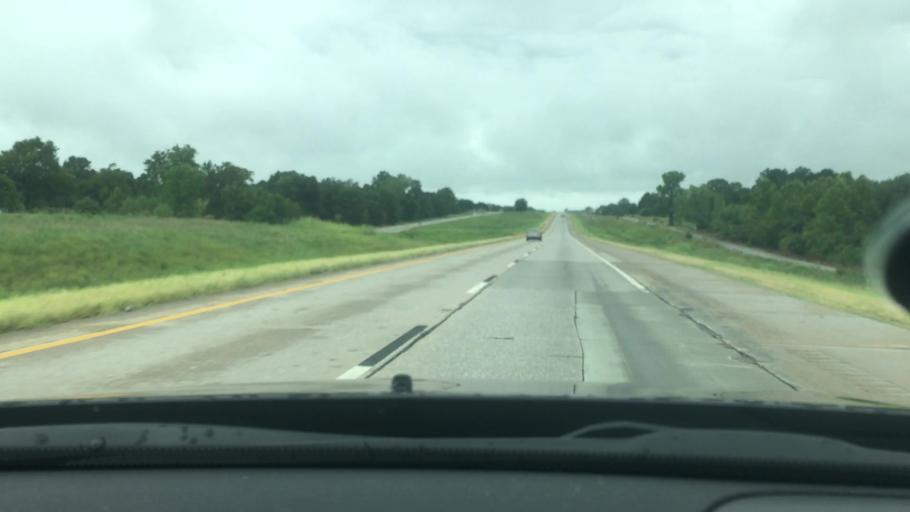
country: US
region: Oklahoma
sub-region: Atoka County
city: Atoka
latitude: 34.2132
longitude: -96.2325
